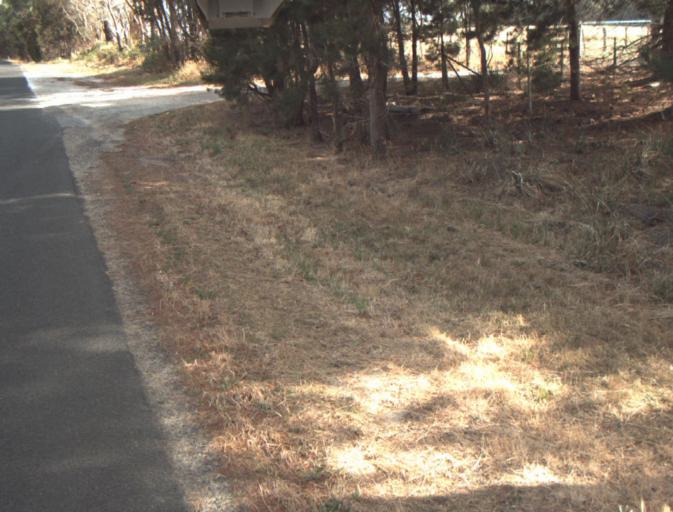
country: AU
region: Tasmania
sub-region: Dorset
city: Bridport
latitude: -41.1086
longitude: 147.2001
